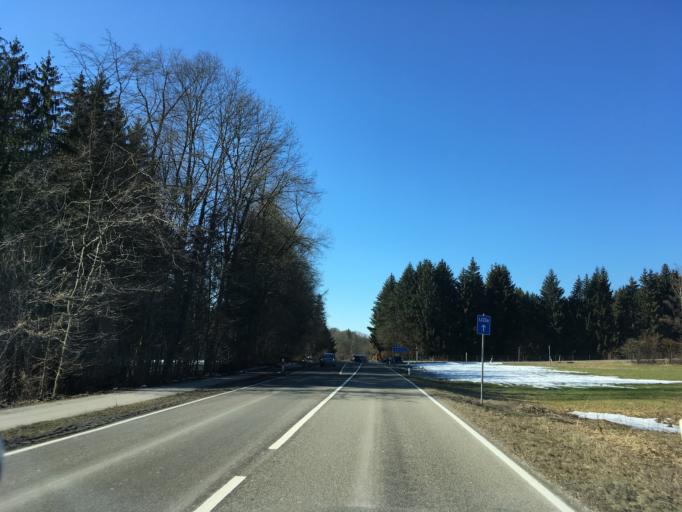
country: DE
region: Bavaria
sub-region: Upper Bavaria
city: Samerberg
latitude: 47.7958
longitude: 12.2151
